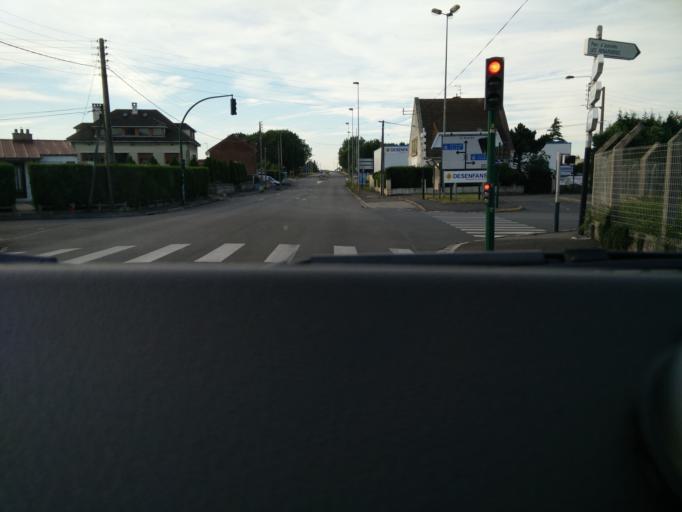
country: FR
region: Nord-Pas-de-Calais
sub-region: Departement du Pas-de-Calais
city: Lens
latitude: 50.4497
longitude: 2.8182
